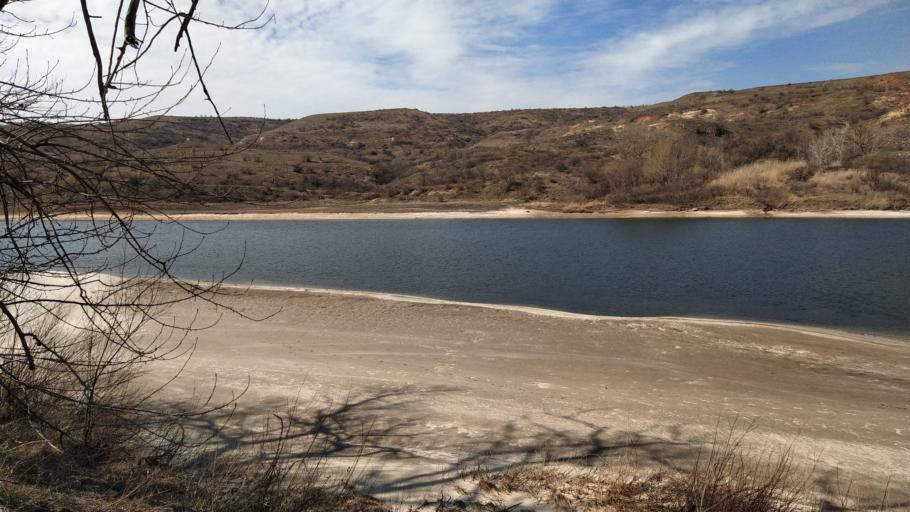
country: RU
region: Rostov
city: Semikarakorsk
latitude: 47.5611
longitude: 40.6744
